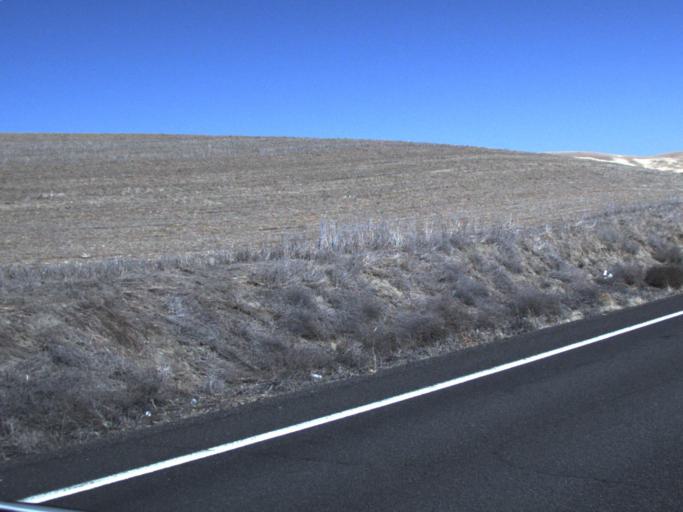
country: US
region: Washington
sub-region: Walla Walla County
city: Garrett
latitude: 46.2903
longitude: -118.5404
